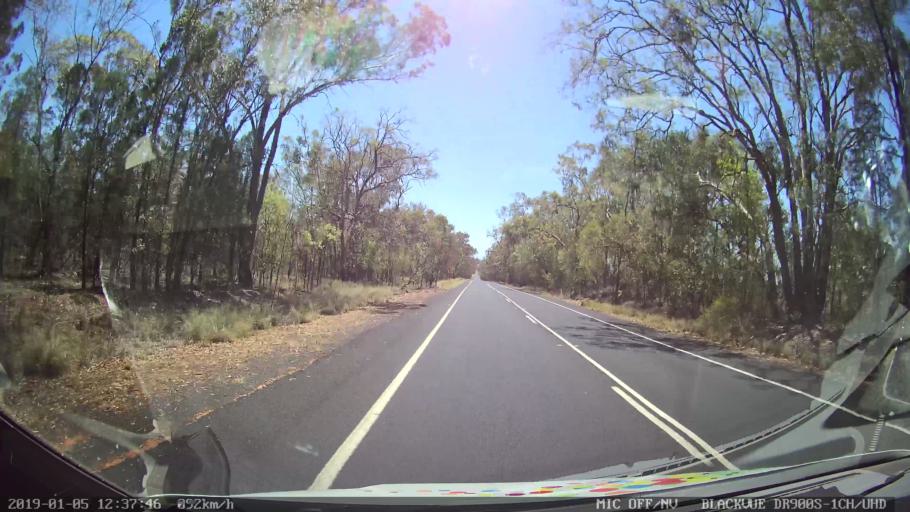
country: AU
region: New South Wales
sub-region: Warrumbungle Shire
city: Coonabarabran
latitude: -31.2013
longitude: 149.4596
